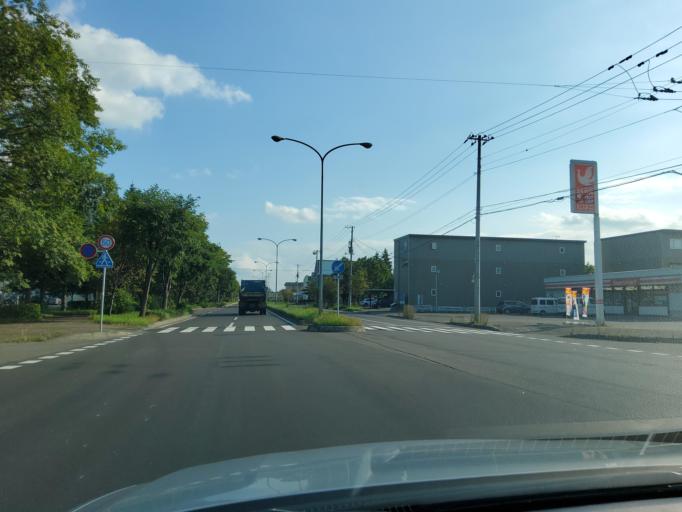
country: JP
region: Hokkaido
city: Obihiro
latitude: 42.9058
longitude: 143.2140
